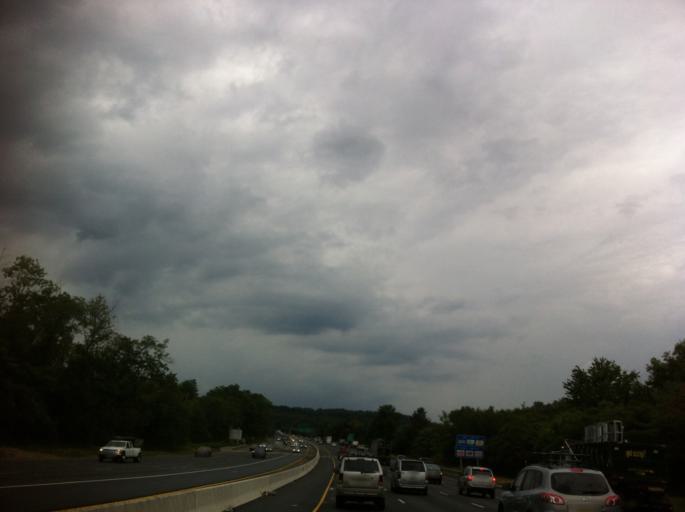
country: US
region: New Jersey
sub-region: Morris County
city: Mountain Lakes
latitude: 40.8742
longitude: -74.4654
